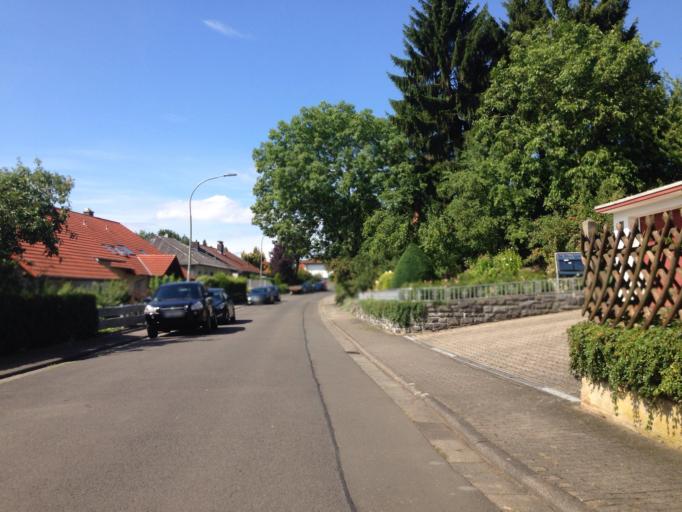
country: DE
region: Hesse
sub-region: Regierungsbezirk Giessen
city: Grunberg
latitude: 50.5890
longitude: 8.9559
